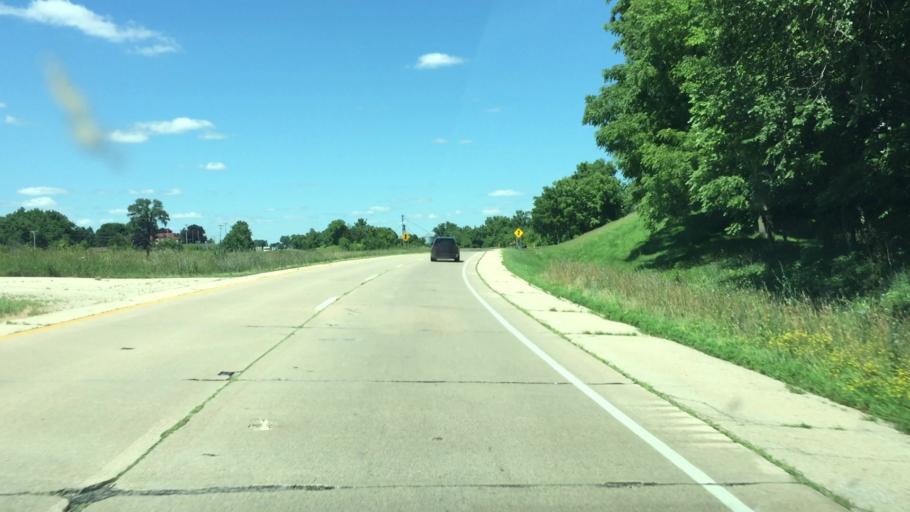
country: US
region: Illinois
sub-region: Jo Daviess County
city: East Dubuque
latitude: 42.5510
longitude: -90.6095
